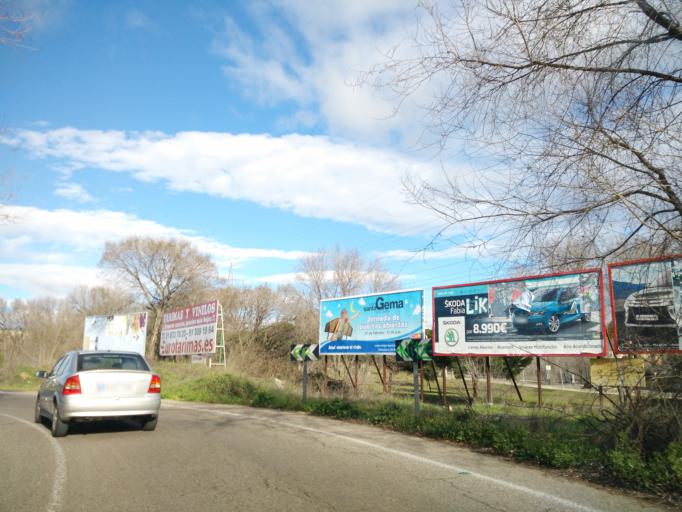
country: ES
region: Madrid
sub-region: Provincia de Madrid
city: Latina
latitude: 40.4001
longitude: -3.7772
